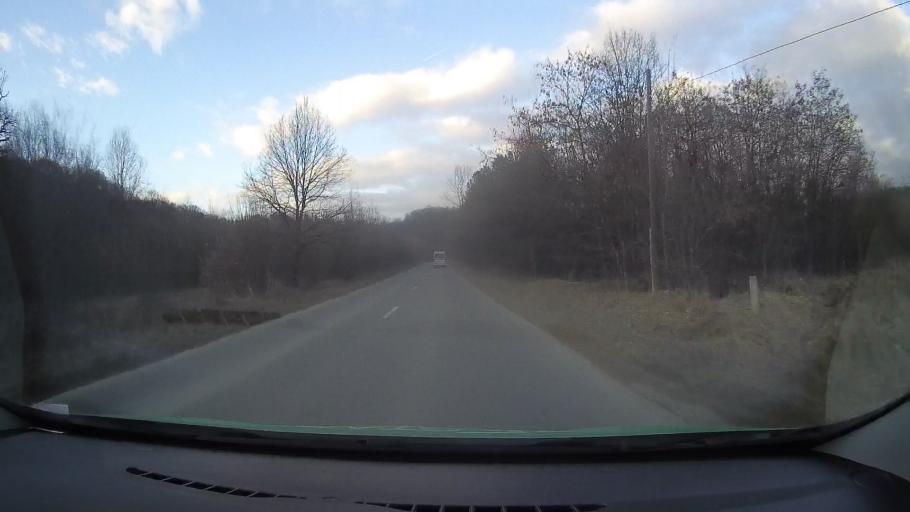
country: RO
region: Dambovita
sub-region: Comuna Gura Ocnitei
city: Gura Ocnitei
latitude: 44.9531
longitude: 25.5964
